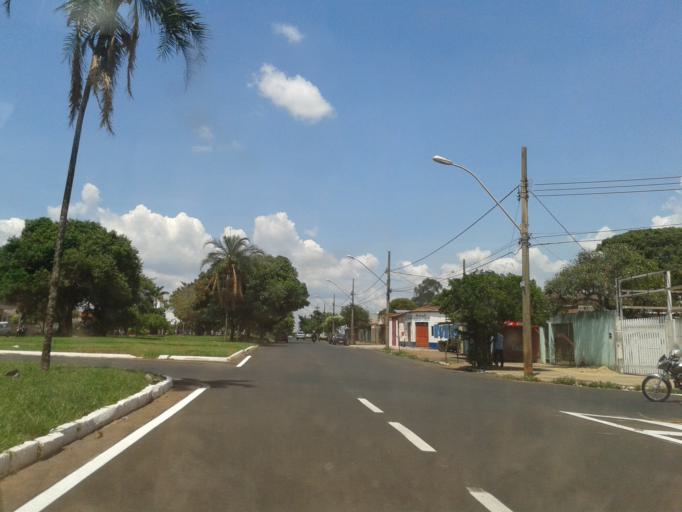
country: BR
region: Minas Gerais
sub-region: Araguari
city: Araguari
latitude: -18.6622
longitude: -48.1947
